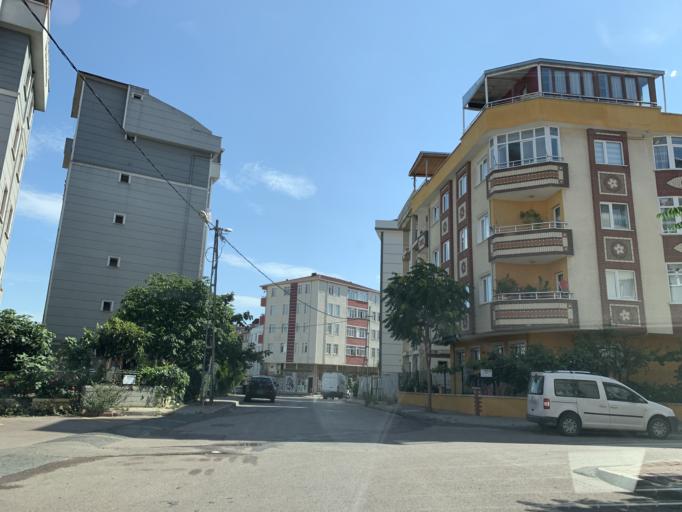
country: TR
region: Istanbul
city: Pendik
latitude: 40.8868
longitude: 29.2693
